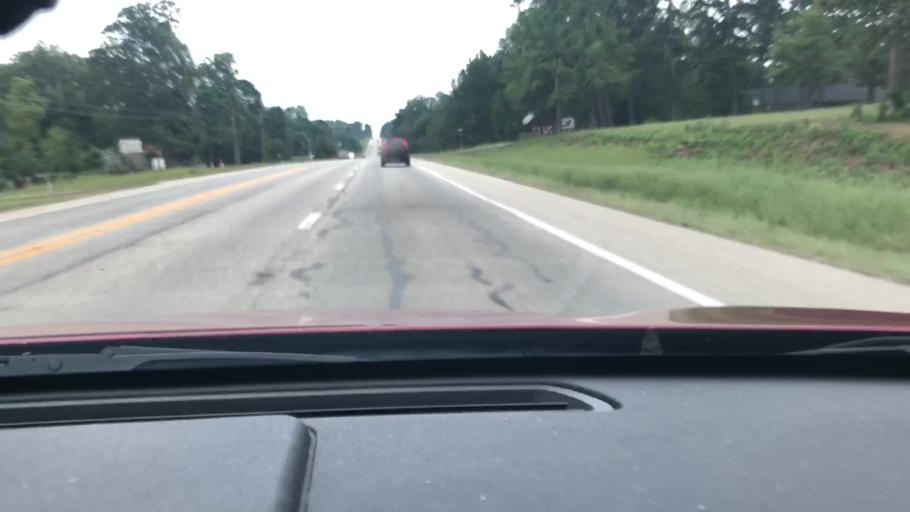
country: US
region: Arkansas
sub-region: Miller County
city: Texarkana
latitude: 33.4296
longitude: -93.9530
